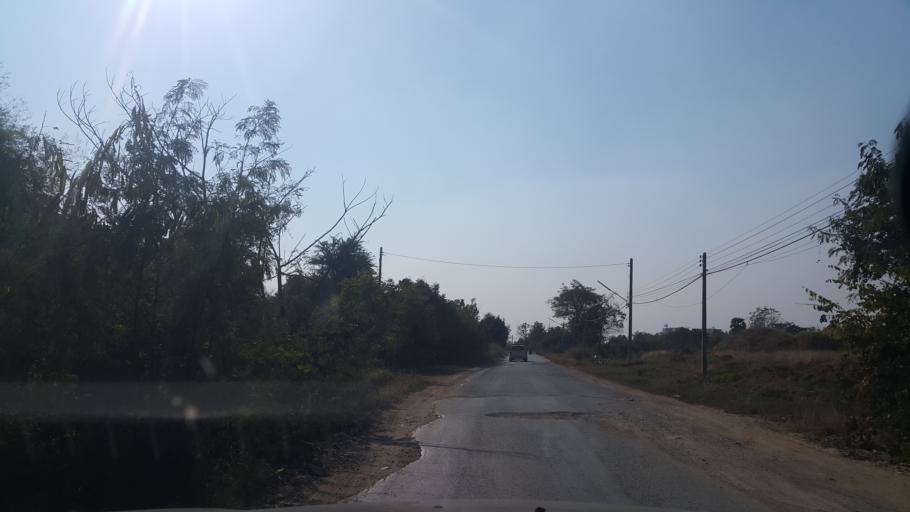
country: TH
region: Nakhon Ratchasima
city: Phimai
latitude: 15.2335
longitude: 102.4885
